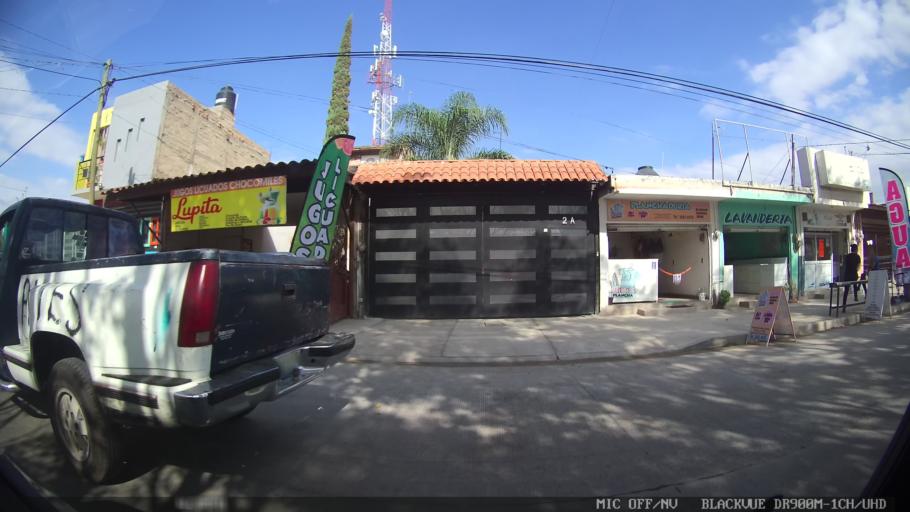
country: MX
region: Jalisco
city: Tonala
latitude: 20.6575
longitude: -103.2510
